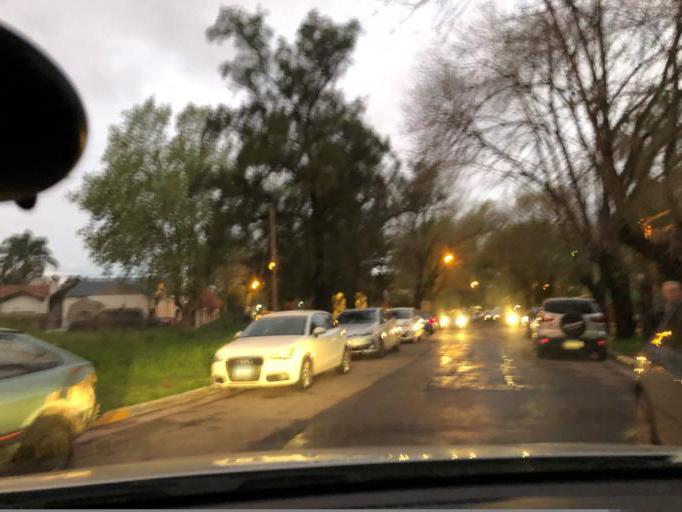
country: AR
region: Buenos Aires
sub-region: Partido de La Plata
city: La Plata
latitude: -34.8676
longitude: -58.0470
